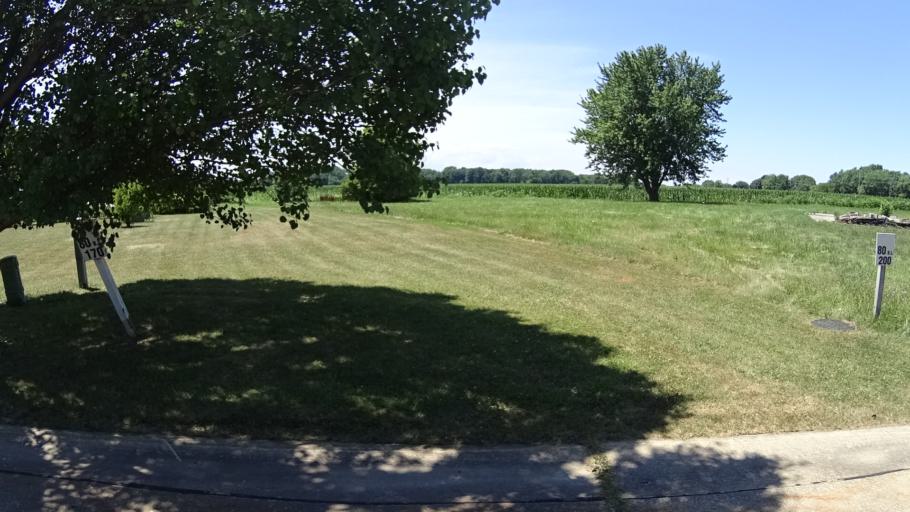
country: US
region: Ohio
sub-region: Erie County
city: Sandusky
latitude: 41.3945
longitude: -82.6580
